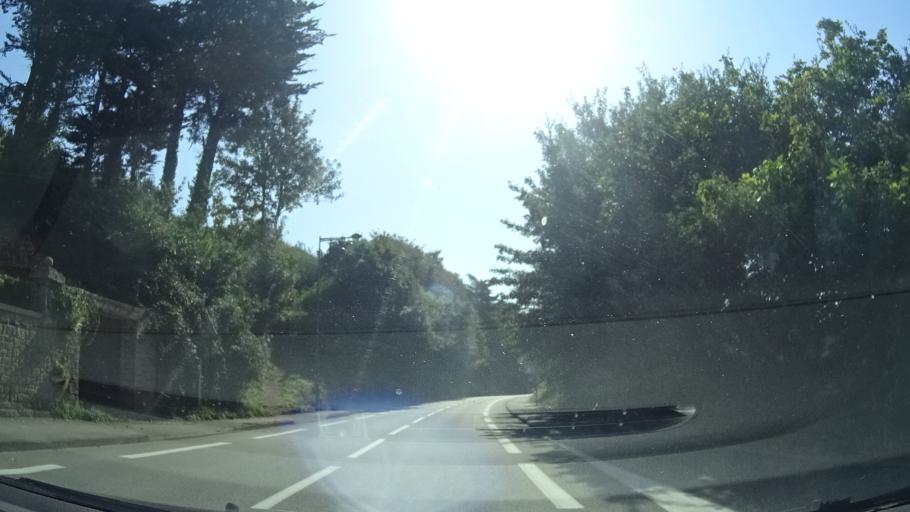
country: FR
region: Brittany
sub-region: Departement du Finistere
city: Douarnenez
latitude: 48.0838
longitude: -4.3297
